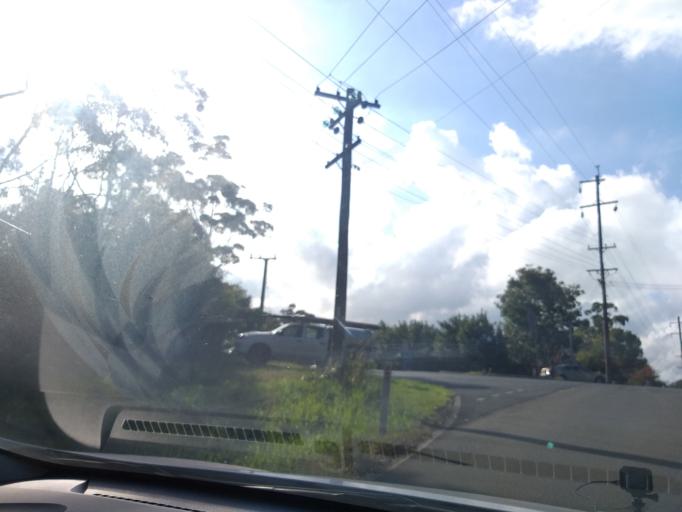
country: AU
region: New South Wales
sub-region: Wollongong
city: Helensburgh
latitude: -34.2112
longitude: 150.9774
